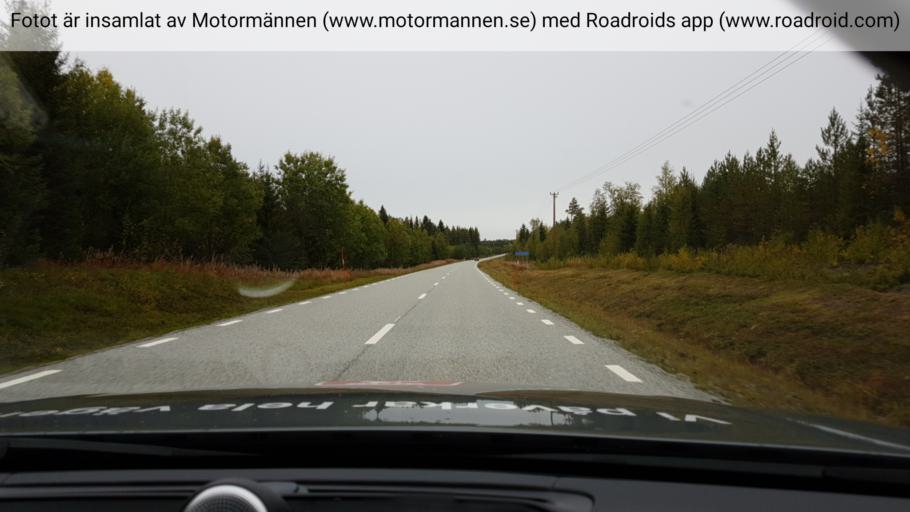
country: SE
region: Jaemtland
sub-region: Stroemsunds Kommun
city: Stroemsund
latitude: 63.9392
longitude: 15.4911
